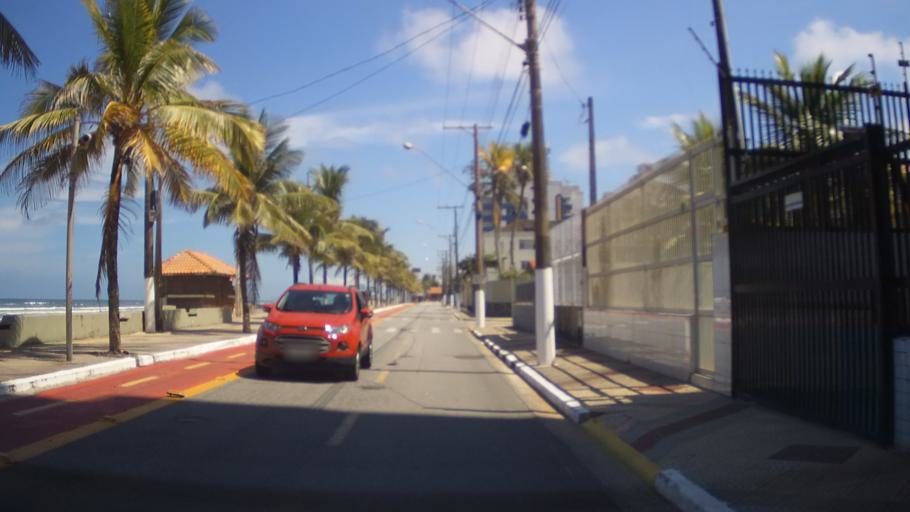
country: BR
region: Sao Paulo
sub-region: Mongagua
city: Mongagua
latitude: -24.0943
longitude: -46.6161
